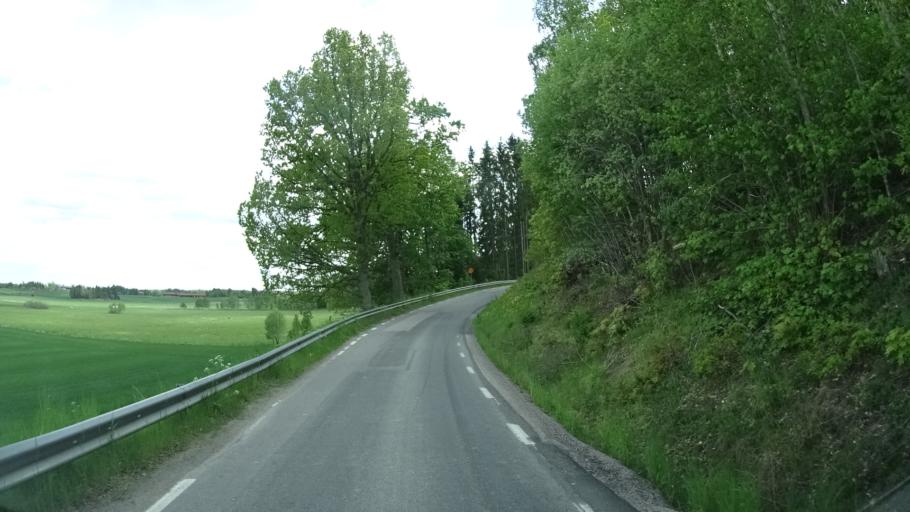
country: SE
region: OEstergoetland
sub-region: Finspangs Kommun
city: Finspang
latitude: 58.5921
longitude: 15.7751
